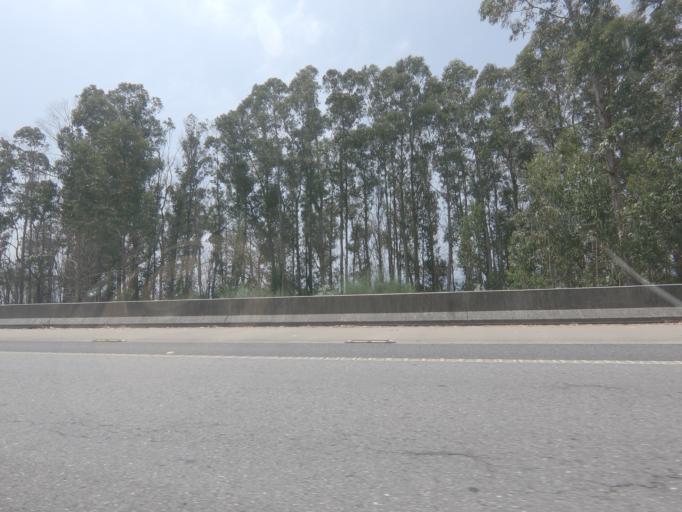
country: ES
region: Galicia
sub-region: Provincia de Pontevedra
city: A Guarda
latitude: 41.9260
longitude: -8.8811
